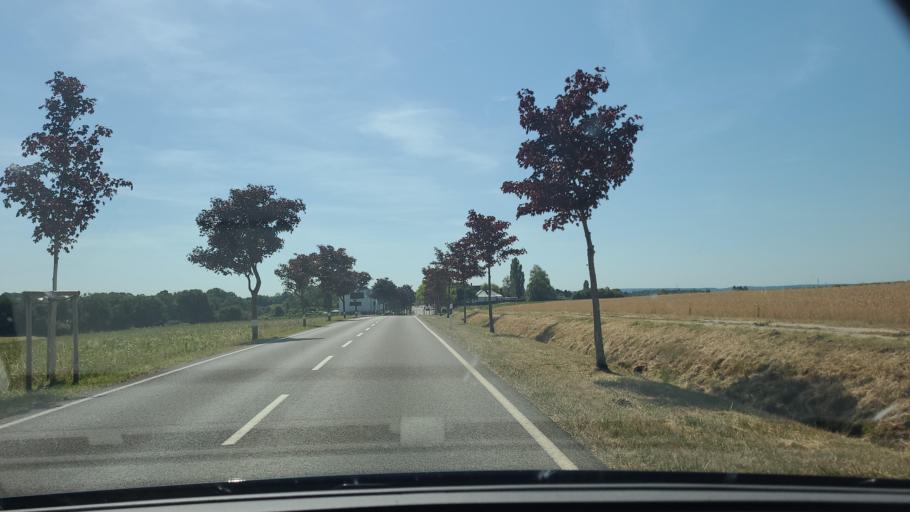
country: LU
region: Luxembourg
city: Schouweiler
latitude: 49.5905
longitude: 5.9495
